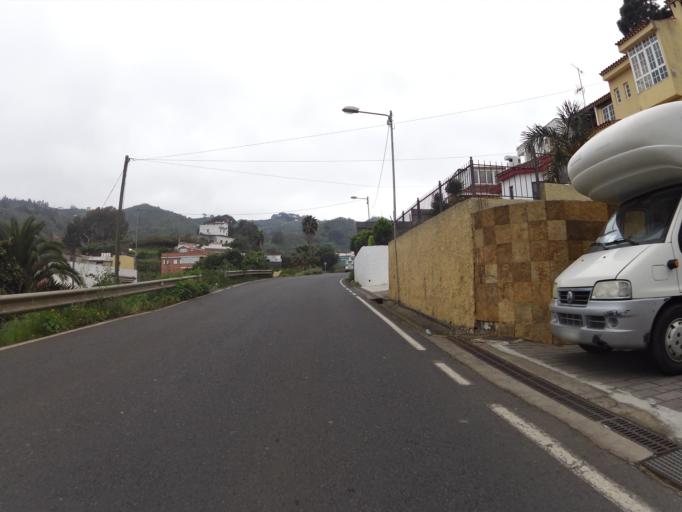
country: ES
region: Canary Islands
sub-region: Provincia de Las Palmas
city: Teror
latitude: 28.0649
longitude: -15.5386
